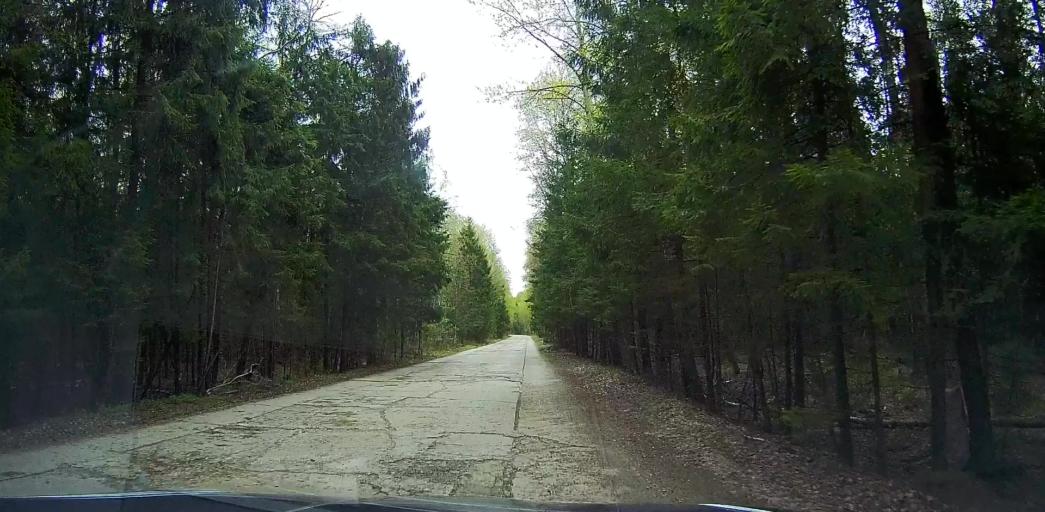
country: RU
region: Moskovskaya
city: Malyshevo
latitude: 55.5364
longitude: 38.3853
